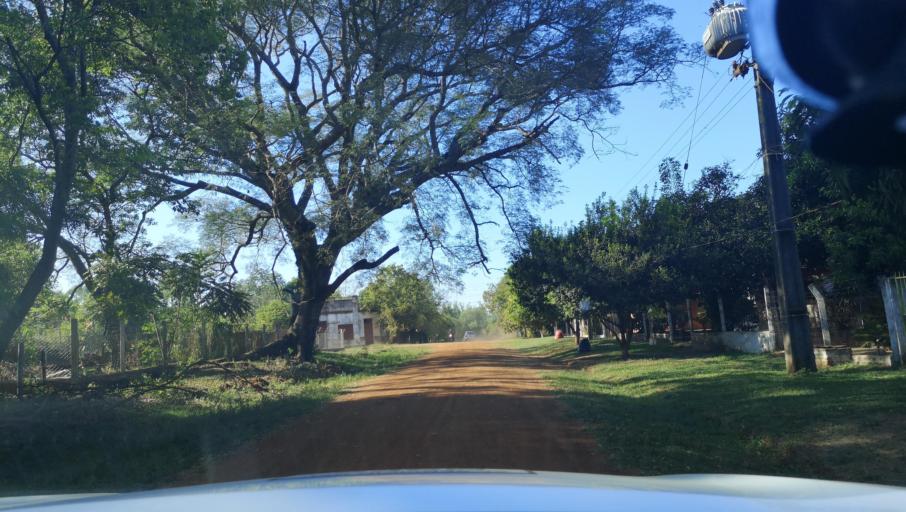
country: PY
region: Itapua
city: Carmen del Parana
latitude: -27.1704
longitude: -56.2406
